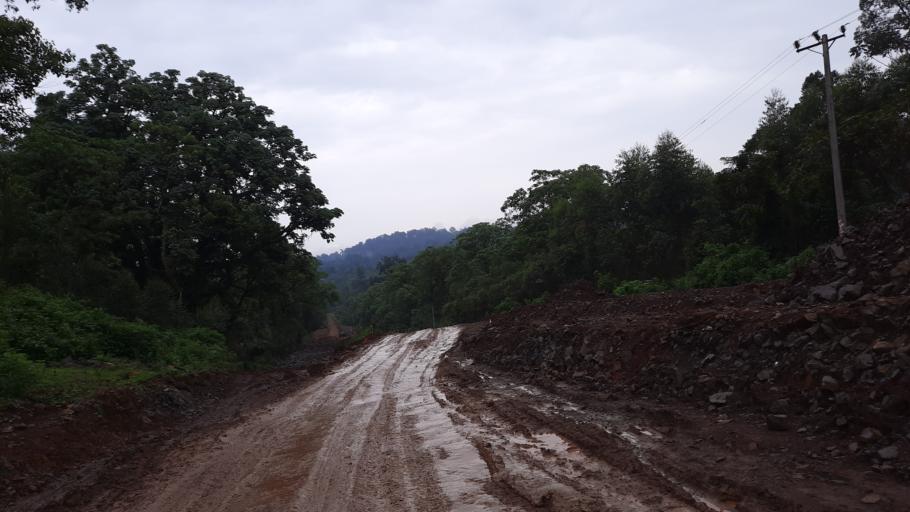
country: ET
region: Oromiya
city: Gore
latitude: 7.8668
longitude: 35.4800
